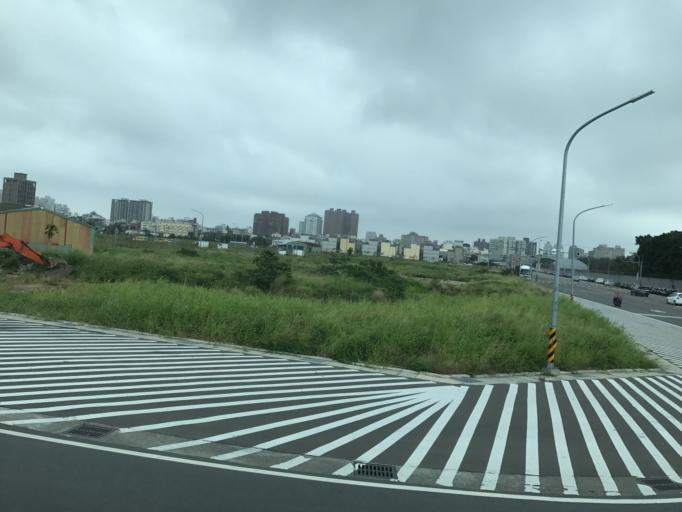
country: TW
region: Taiwan
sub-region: Hsinchu
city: Hsinchu
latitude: 24.8216
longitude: 120.9521
